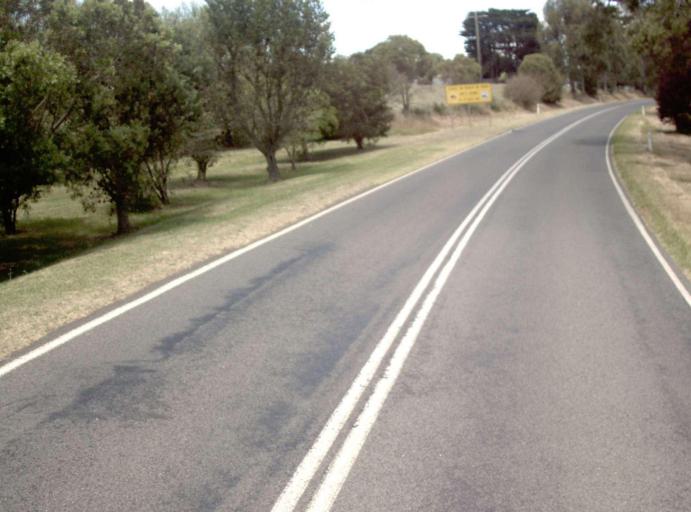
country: AU
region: Victoria
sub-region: Baw Baw
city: Warragul
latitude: -38.2098
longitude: 145.9233
